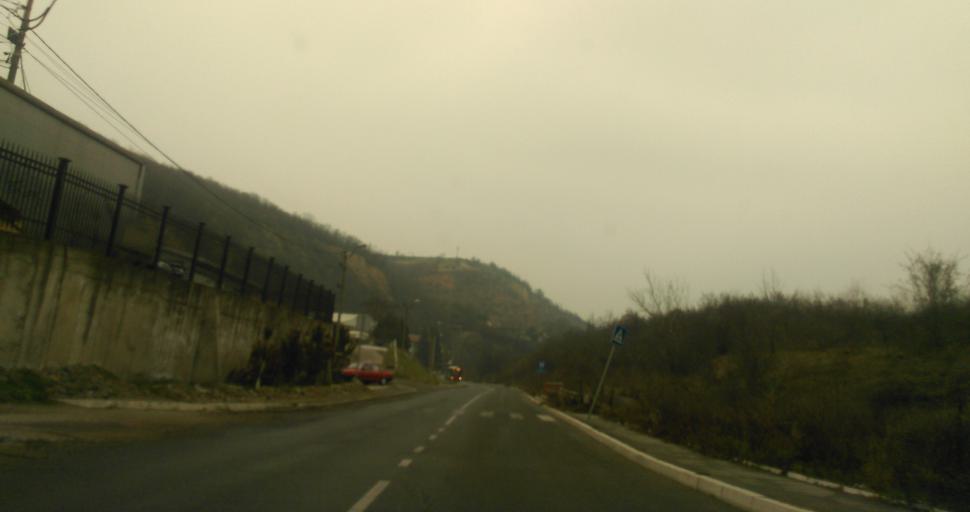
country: RS
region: Central Serbia
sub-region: Belgrade
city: Rakovica
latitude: 44.7270
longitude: 20.4485
